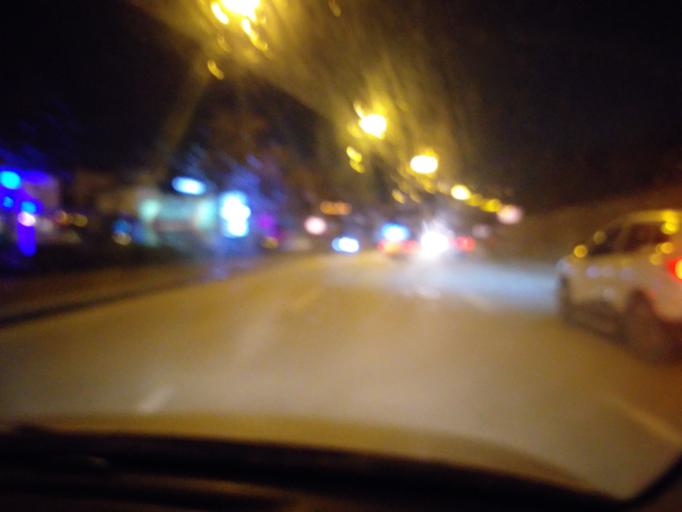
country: TR
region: Ankara
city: Batikent
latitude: 39.8906
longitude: 32.7220
